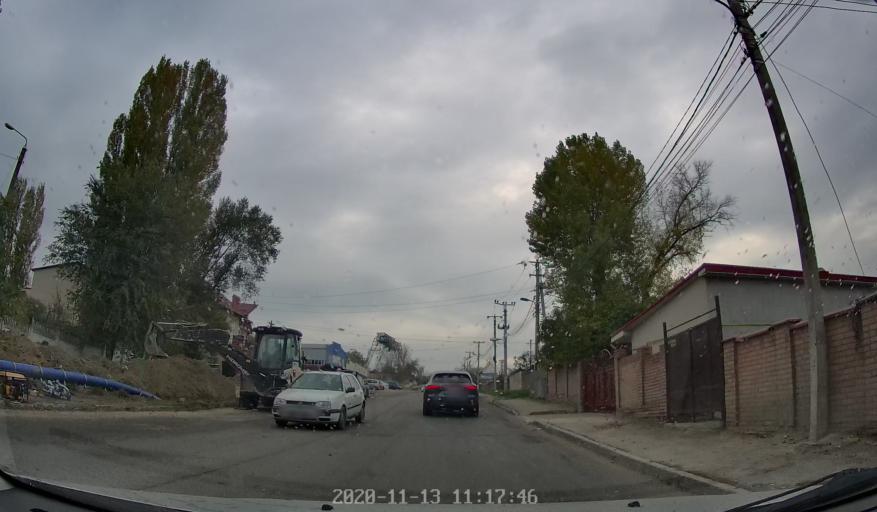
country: MD
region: Chisinau
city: Chisinau
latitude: 46.9929
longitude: 28.9099
